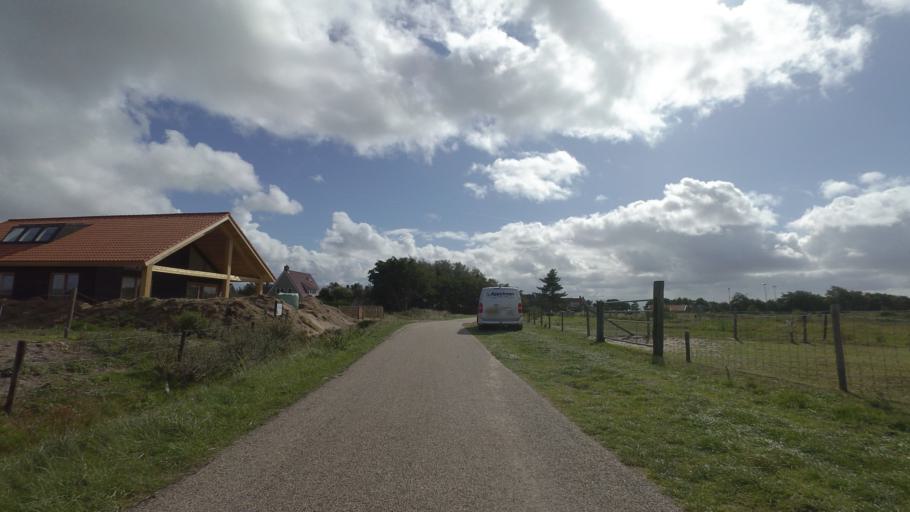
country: NL
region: Friesland
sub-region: Gemeente Ameland
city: Nes
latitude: 53.4500
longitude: 5.7935
